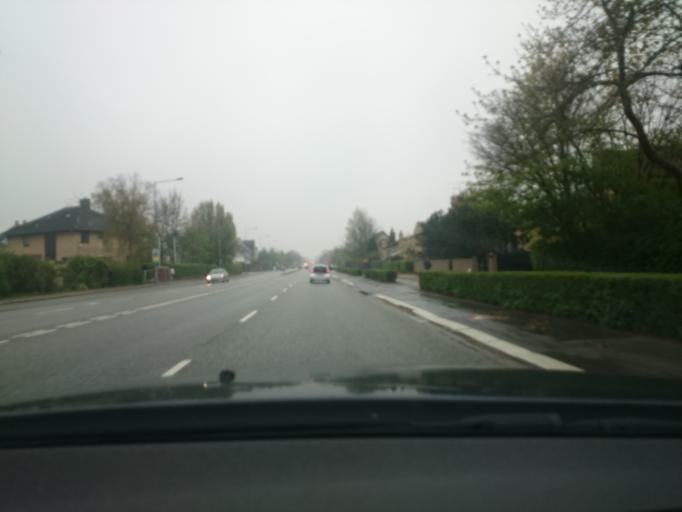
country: DK
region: Capital Region
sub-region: Gentofte Kommune
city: Charlottenlund
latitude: 55.7534
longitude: 12.5578
